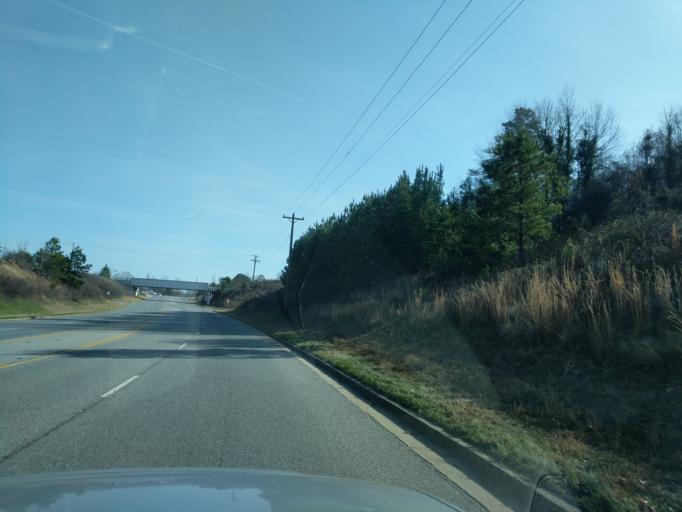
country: US
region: South Carolina
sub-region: Spartanburg County
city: Woodruff
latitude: 34.7526
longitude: -82.0511
